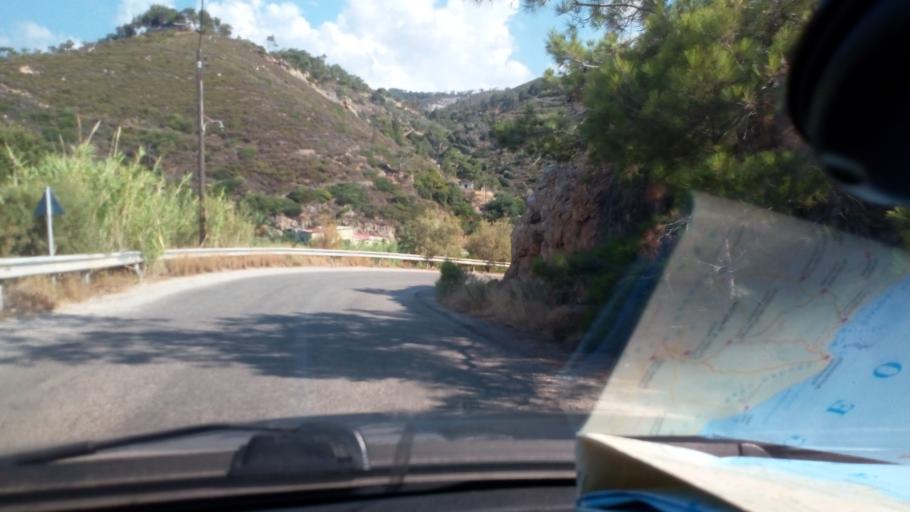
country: GR
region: North Aegean
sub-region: Nomos Samou
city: Agios Kirykos
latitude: 37.6291
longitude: 26.0890
